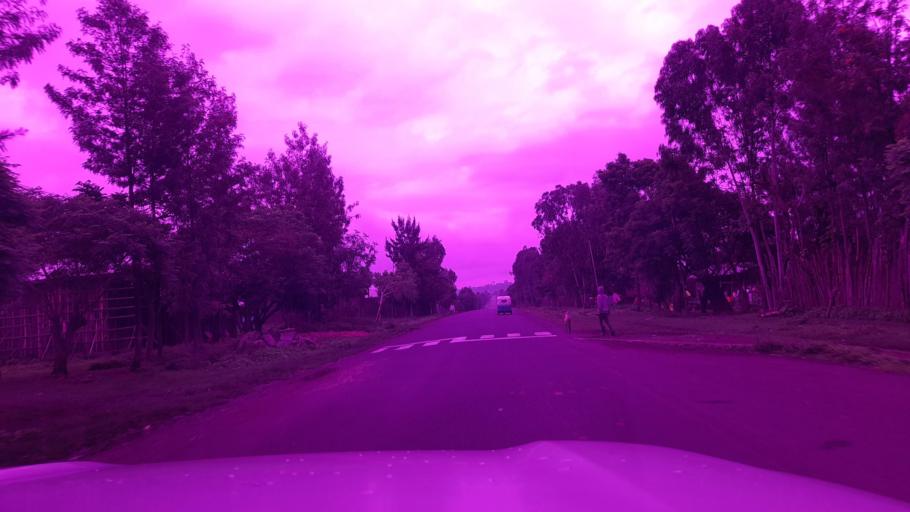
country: ET
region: Oromiya
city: Waliso
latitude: 8.2807
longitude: 37.6887
